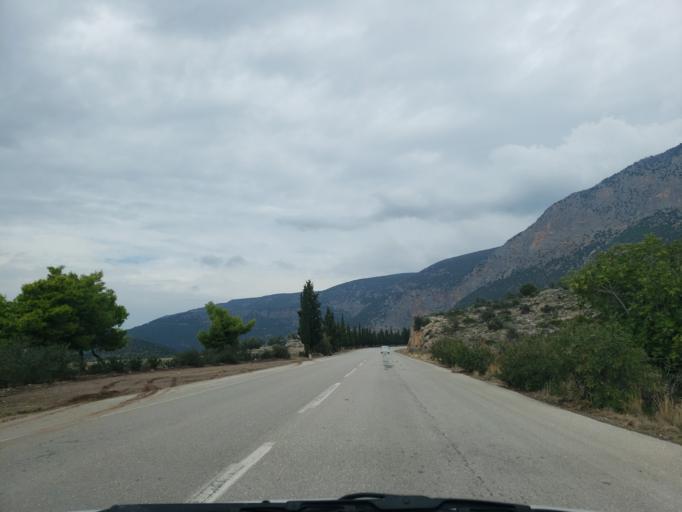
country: GR
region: Central Greece
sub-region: Nomos Fokidos
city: Delphi
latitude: 38.4800
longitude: 22.4622
